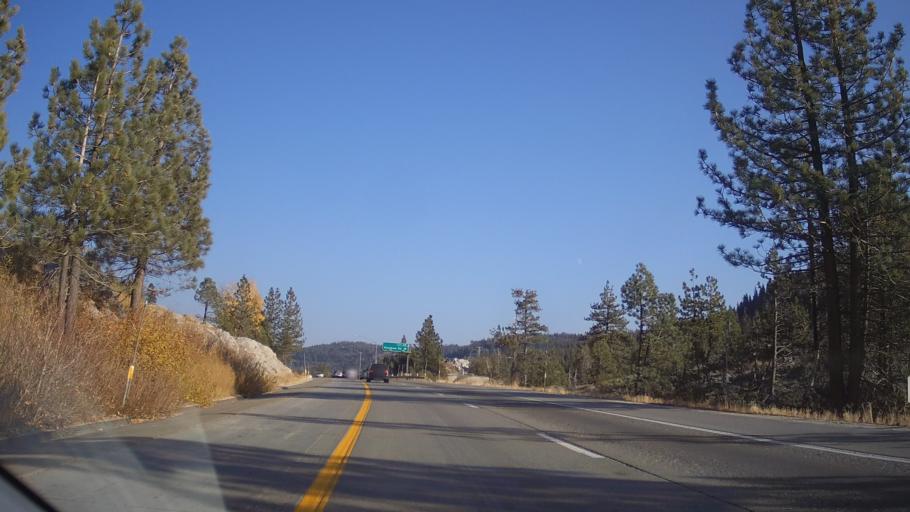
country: US
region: California
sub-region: Nevada County
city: Truckee
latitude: 39.3119
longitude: -120.5059
